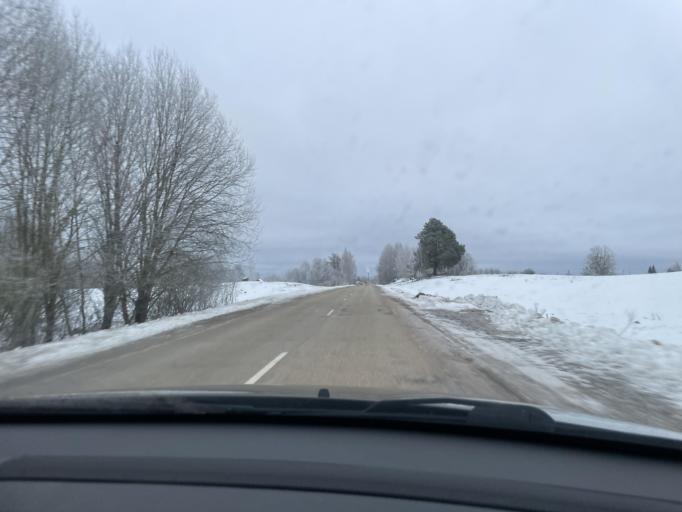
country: LV
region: Ludzas Rajons
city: Ludza
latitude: 56.4370
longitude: 27.5334
